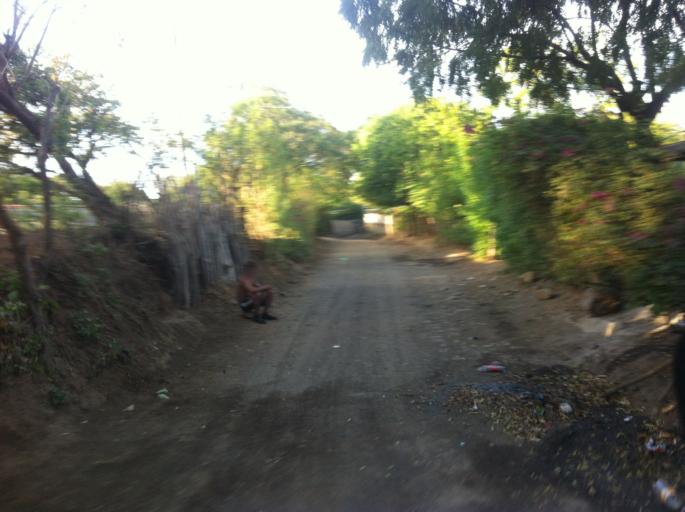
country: NI
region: Managua
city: Managua
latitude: 12.0822
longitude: -86.3109
